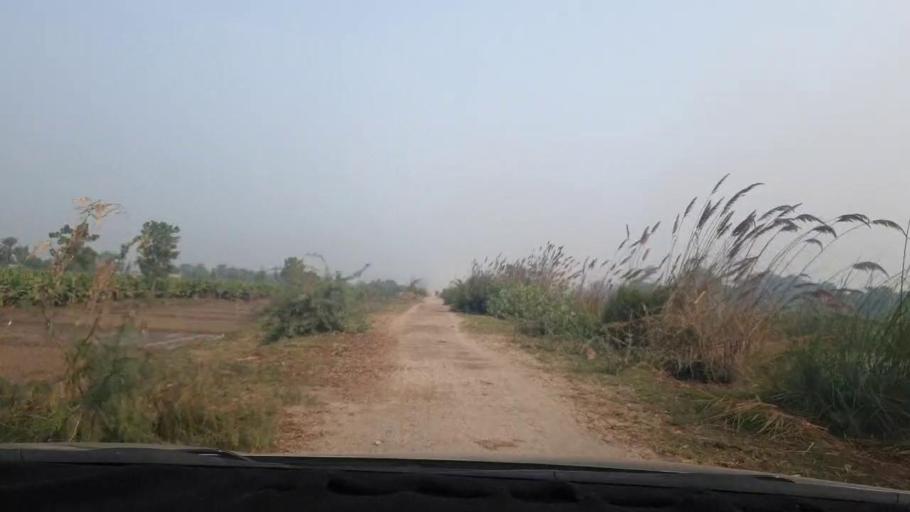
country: PK
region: Sindh
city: Matiari
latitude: 25.5927
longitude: 68.5495
